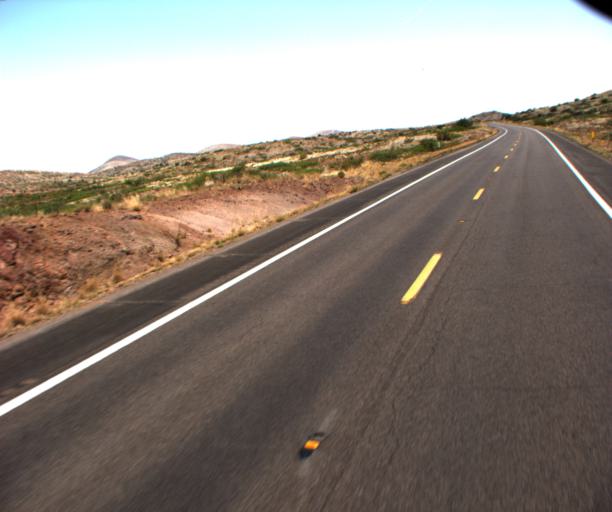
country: US
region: Arizona
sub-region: Greenlee County
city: Clifton
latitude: 32.7648
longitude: -109.2519
